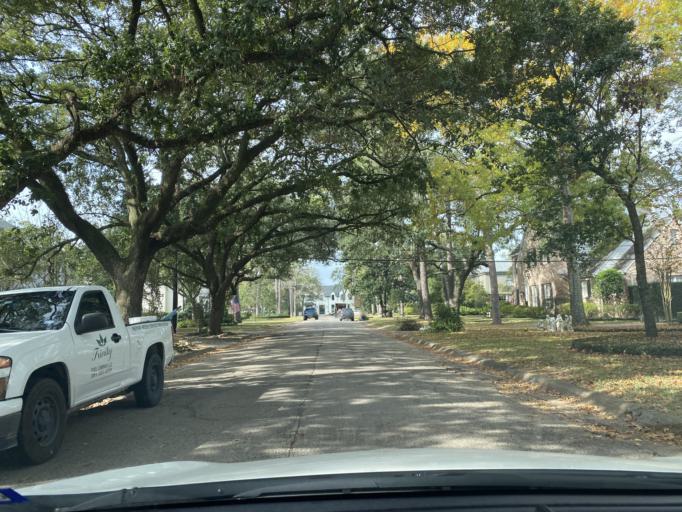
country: US
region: Texas
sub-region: Harris County
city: Hunters Creek Village
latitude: 29.7654
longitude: -95.4692
